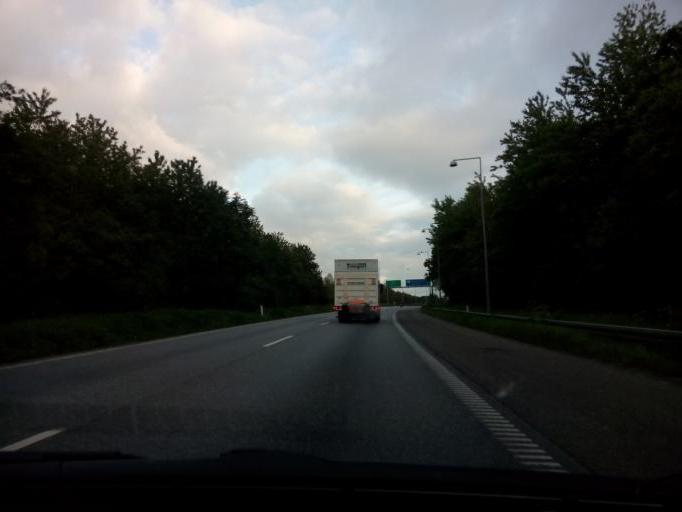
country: DK
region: North Denmark
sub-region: Alborg Kommune
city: Aalborg
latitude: 57.0491
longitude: 9.9703
